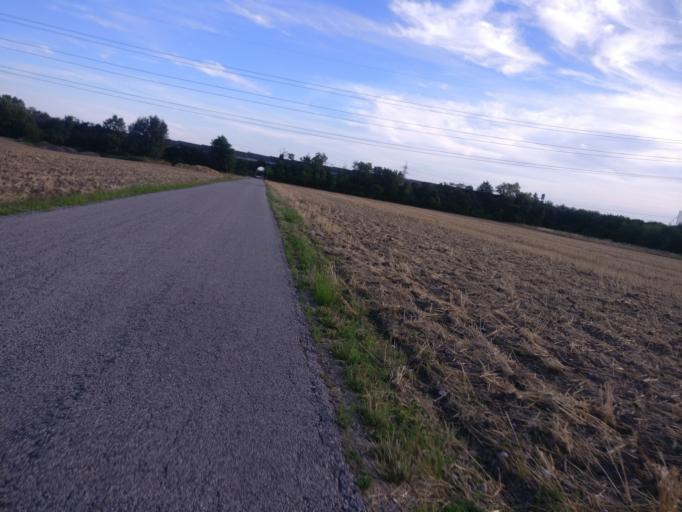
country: AT
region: Lower Austria
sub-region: Politischer Bezirk Modling
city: Biedermannsdorf
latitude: 48.0800
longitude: 16.3390
